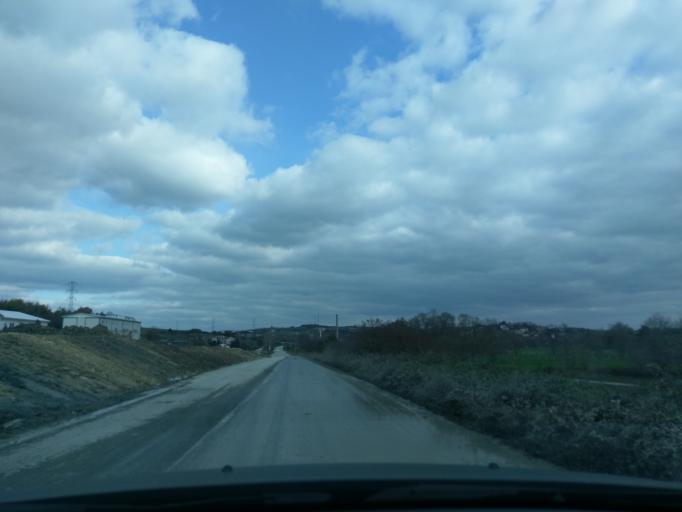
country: TR
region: Istanbul
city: Durusu
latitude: 41.2929
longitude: 28.6663
